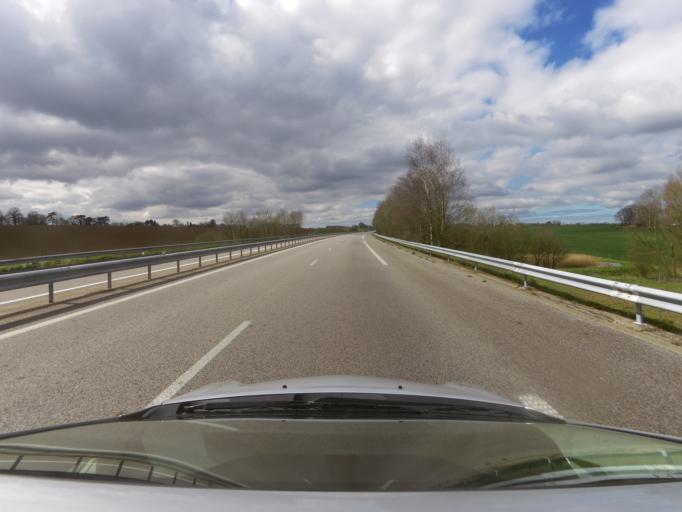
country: FR
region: Haute-Normandie
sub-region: Departement de la Seine-Maritime
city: Beuzeville-la-Grenier
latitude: 49.5694
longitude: 0.3919
